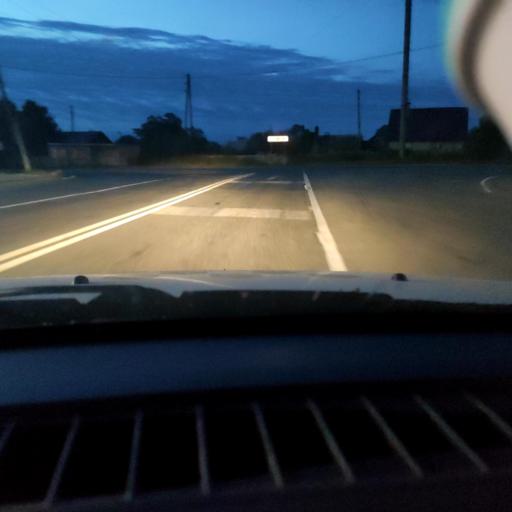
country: RU
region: Kirov
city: Kotel'nich
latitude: 58.3191
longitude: 48.3971
